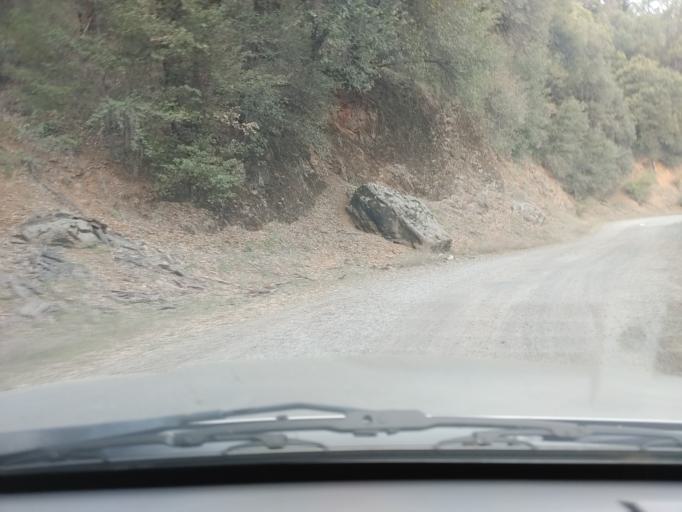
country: US
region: California
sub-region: Shasta County
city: Bella Vista
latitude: 40.8390
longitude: -122.0247
